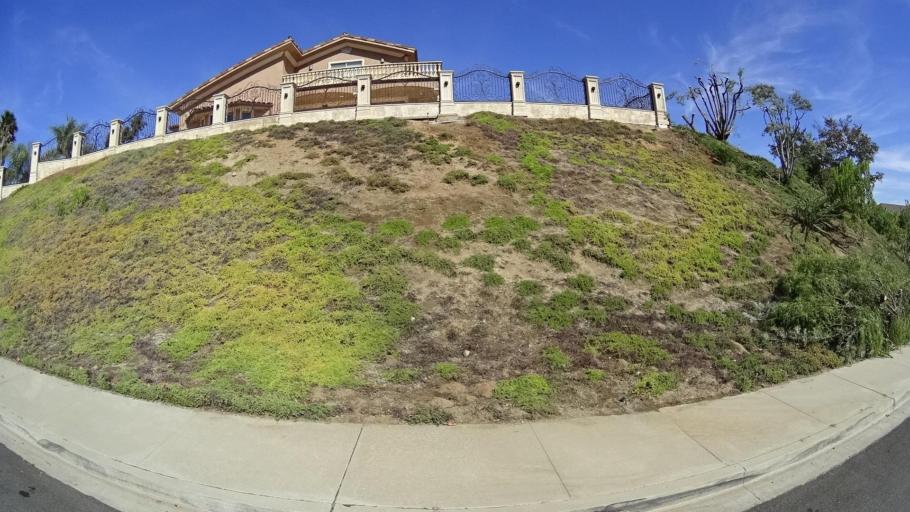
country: US
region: California
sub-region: San Diego County
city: Rancho San Diego
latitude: 32.7579
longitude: -116.9470
